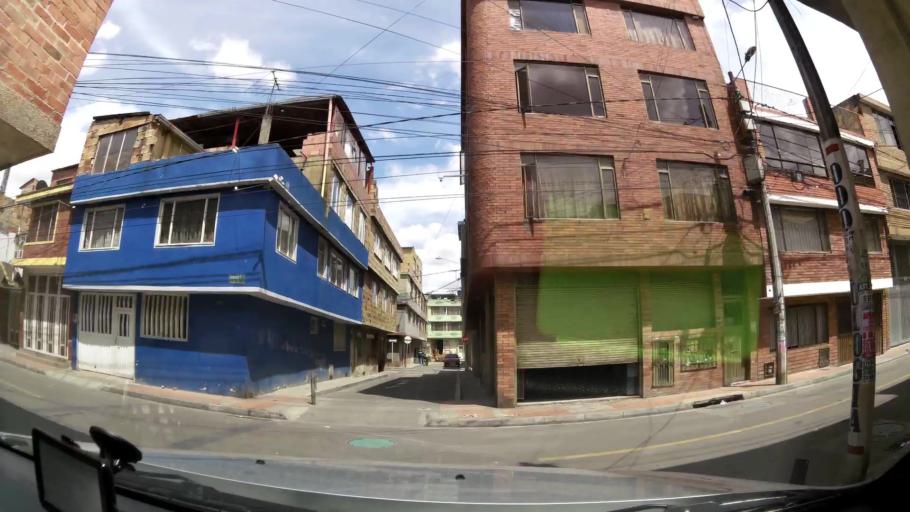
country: CO
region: Bogota D.C.
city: Bogota
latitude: 4.6539
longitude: -74.1384
